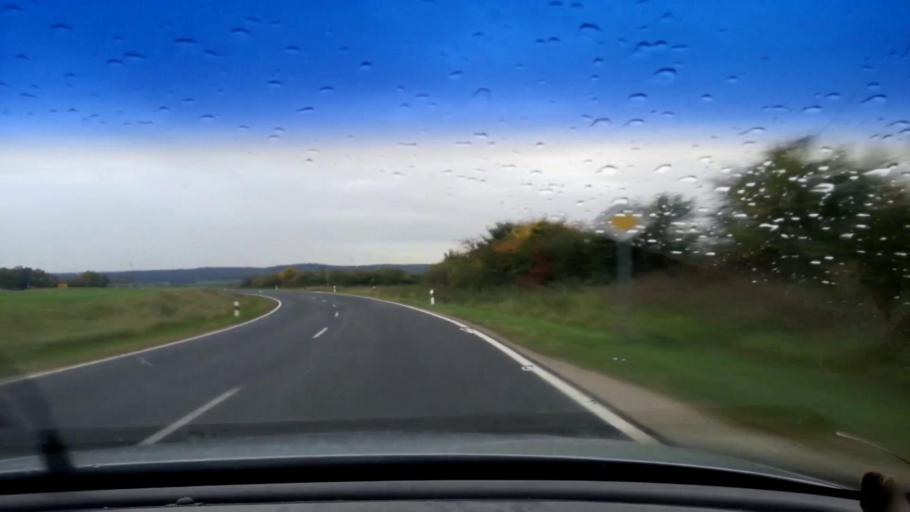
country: DE
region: Bavaria
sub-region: Upper Franconia
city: Priesendorf
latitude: 49.8649
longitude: 10.7176
